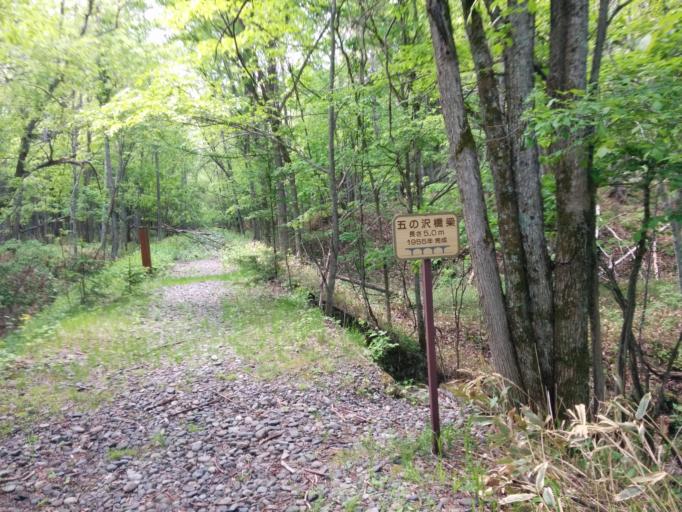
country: JP
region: Hokkaido
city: Otofuke
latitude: 43.4003
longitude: 143.1826
